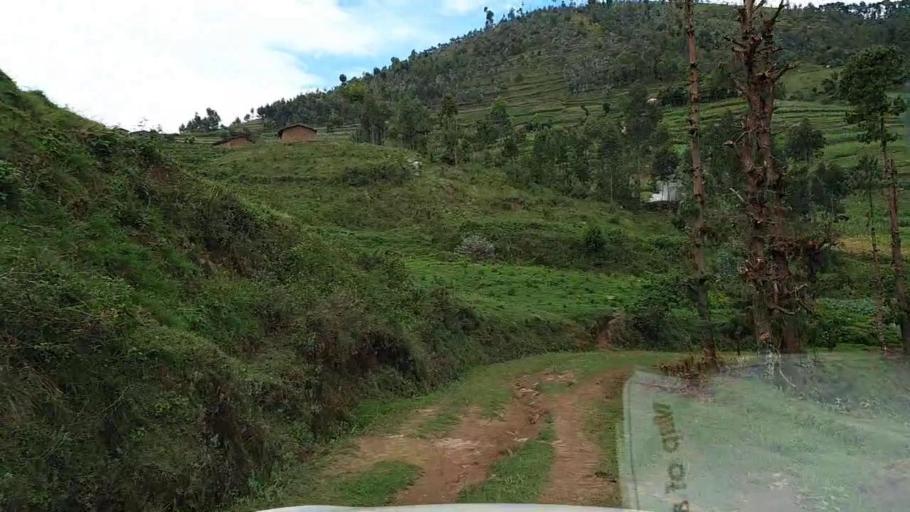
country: RW
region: Southern Province
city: Nzega
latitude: -2.4044
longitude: 29.4991
